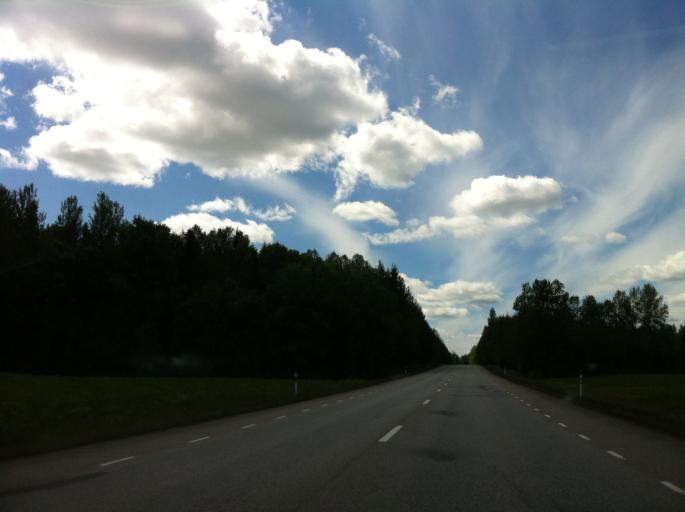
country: SE
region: Vaestra Goetaland
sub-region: Amals Kommun
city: Amal
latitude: 59.0006
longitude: 12.6827
